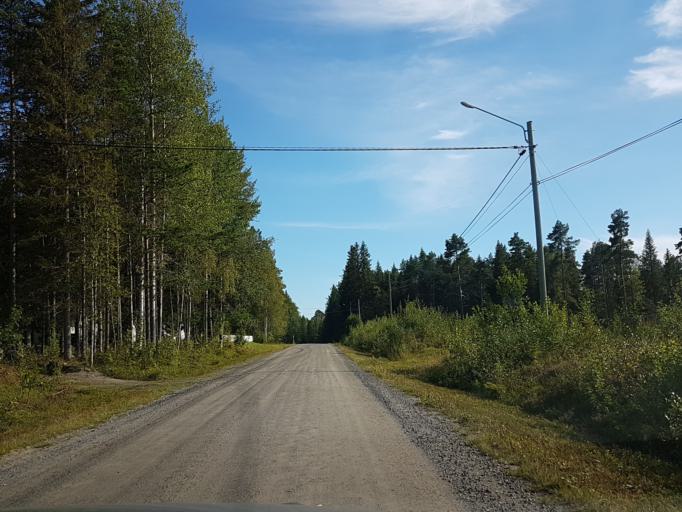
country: SE
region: Vaesterbotten
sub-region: Robertsfors Kommun
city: Robertsfors
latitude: 64.0555
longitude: 20.8705
